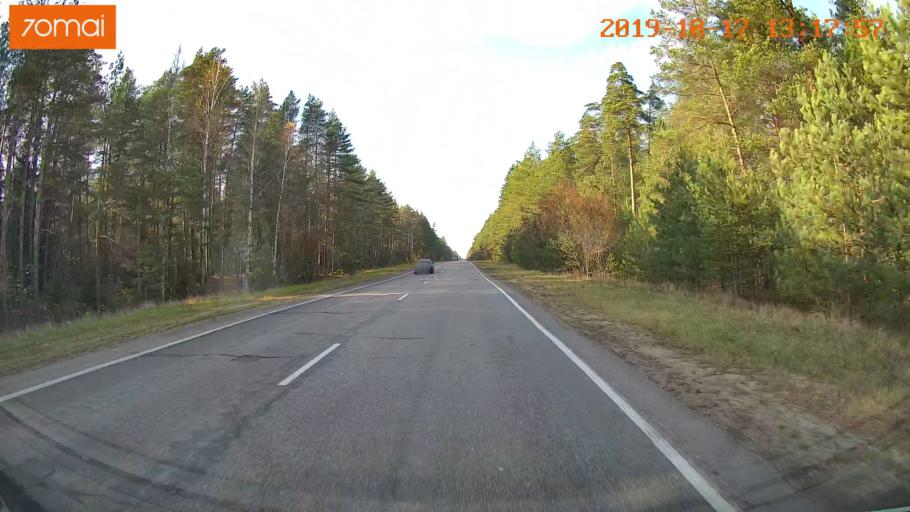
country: RU
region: Rjazan
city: Gus'-Zheleznyy
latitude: 55.0600
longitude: 41.1091
